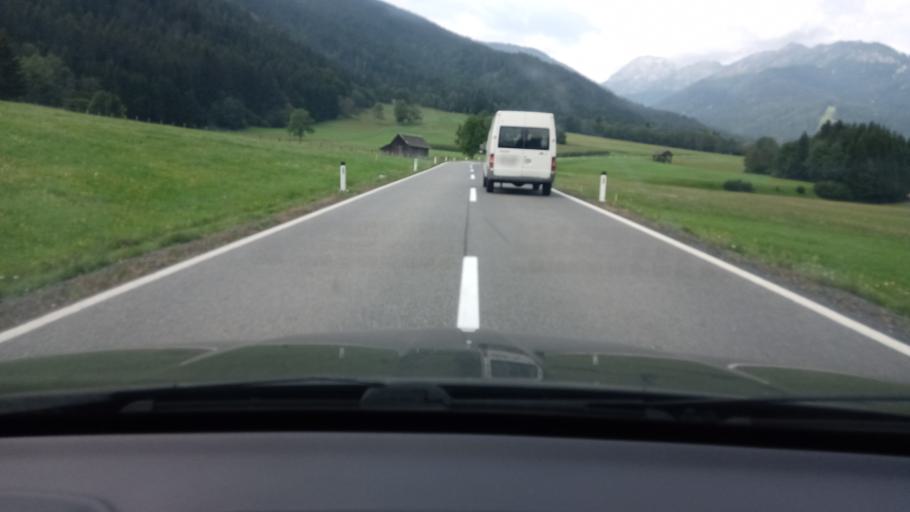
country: AT
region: Carinthia
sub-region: Politischer Bezirk Spittal an der Drau
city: Steinfeld
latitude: 46.6722
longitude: 13.2803
